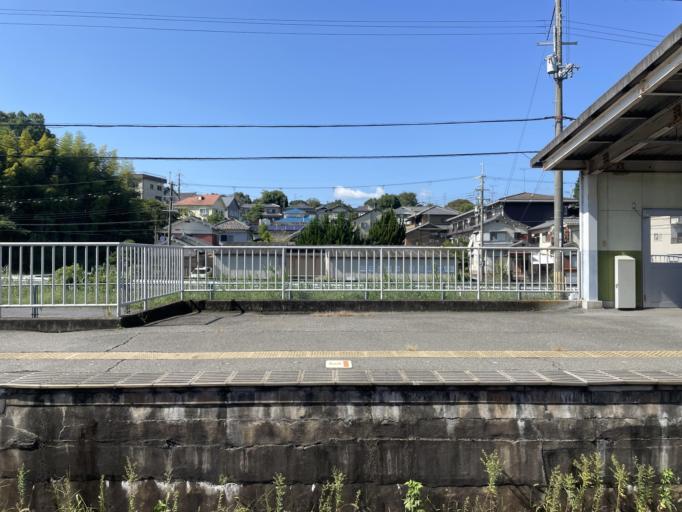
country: JP
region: Nara
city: Kashihara-shi
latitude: 34.4739
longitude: 135.7961
